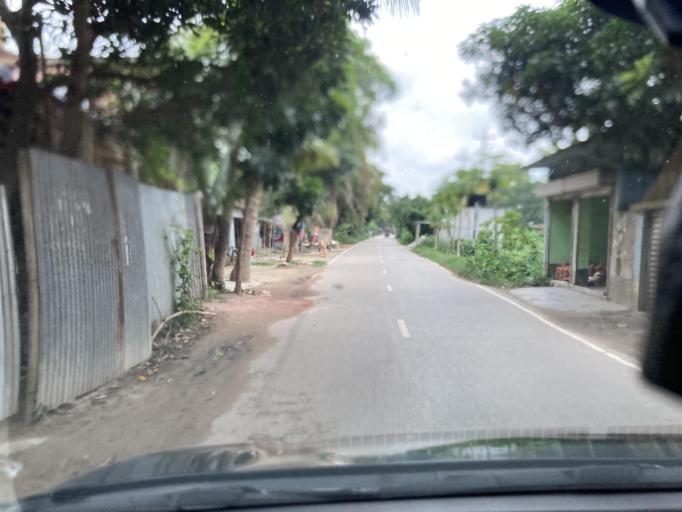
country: BD
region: Dhaka
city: Azimpur
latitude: 23.7697
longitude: 90.2032
